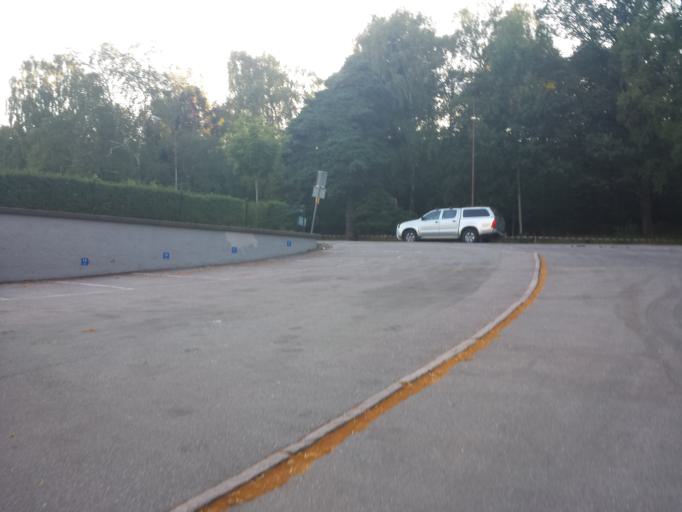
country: SE
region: Stockholm
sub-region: Stockholms Kommun
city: OEstermalm
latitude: 59.3501
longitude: 18.0829
